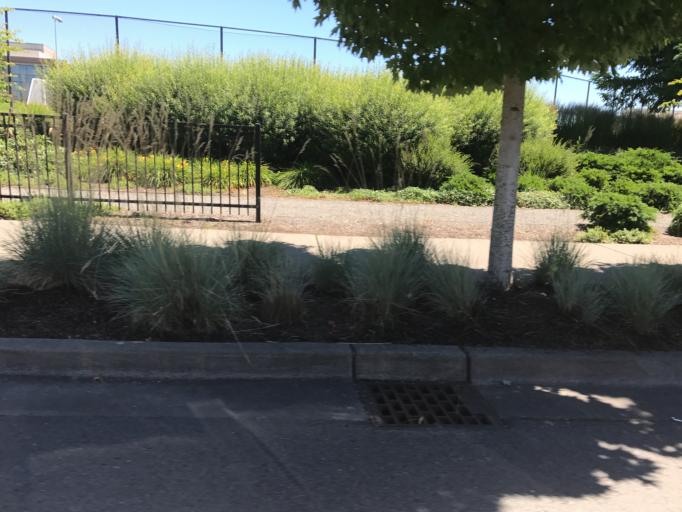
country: US
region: Washington
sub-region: King County
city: Redmond
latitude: 47.6438
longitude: -122.1400
